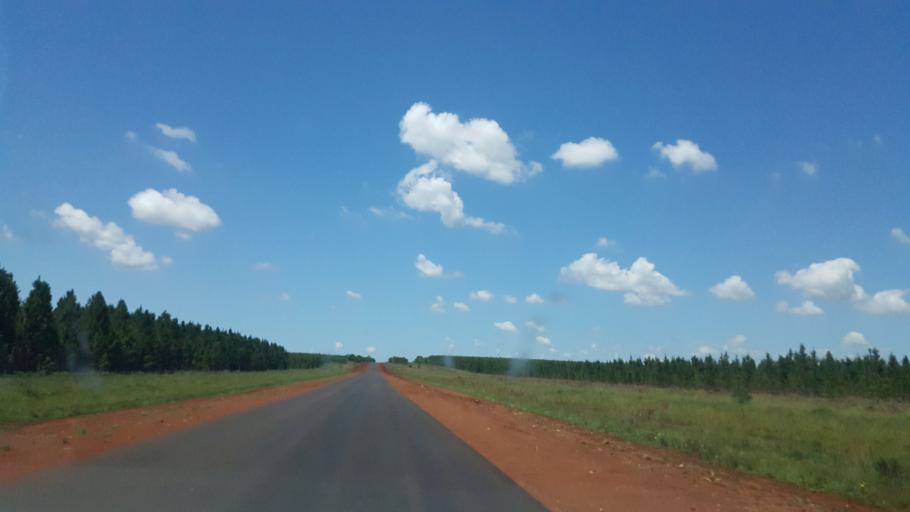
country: AR
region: Corrientes
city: Santo Tome
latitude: -28.4853
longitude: -56.0402
